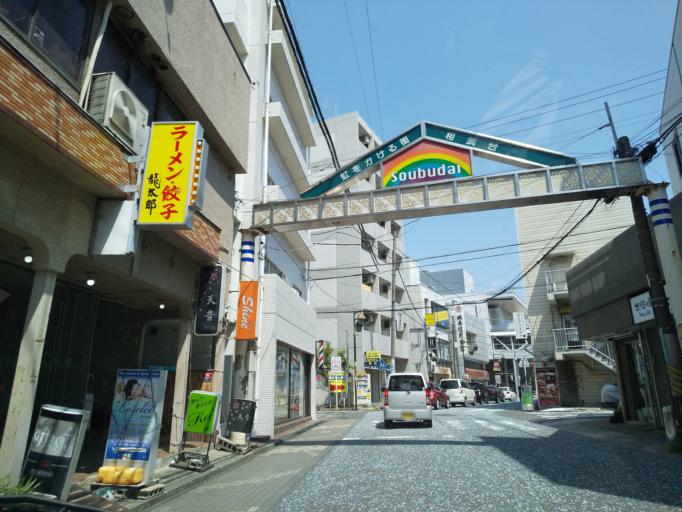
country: JP
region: Kanagawa
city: Zama
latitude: 35.4996
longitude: 139.4070
